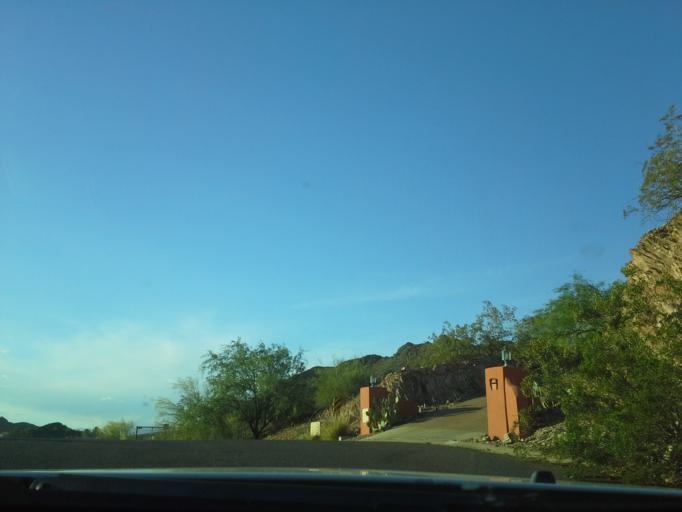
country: US
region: Arizona
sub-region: Maricopa County
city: Paradise Valley
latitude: 33.5729
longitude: -112.0425
